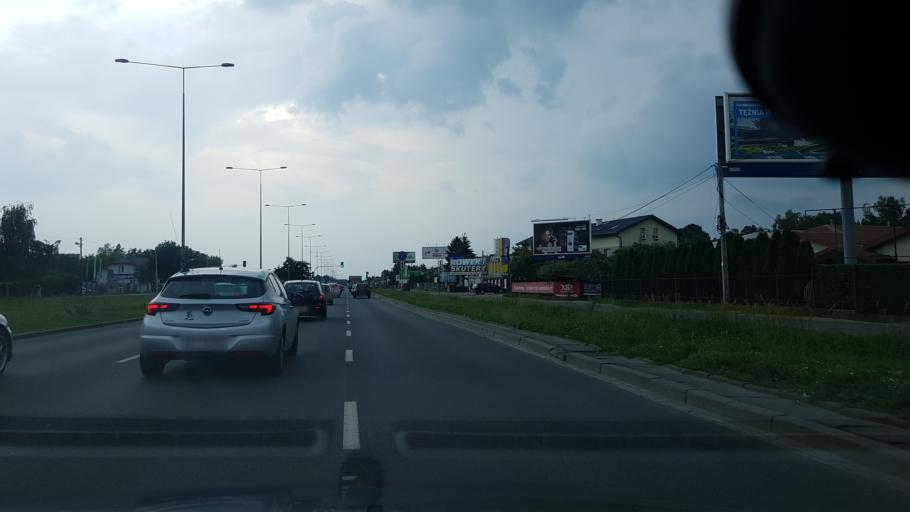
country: PL
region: Masovian Voivodeship
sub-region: Warszawa
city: Bialoleka
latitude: 52.3370
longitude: 20.9595
